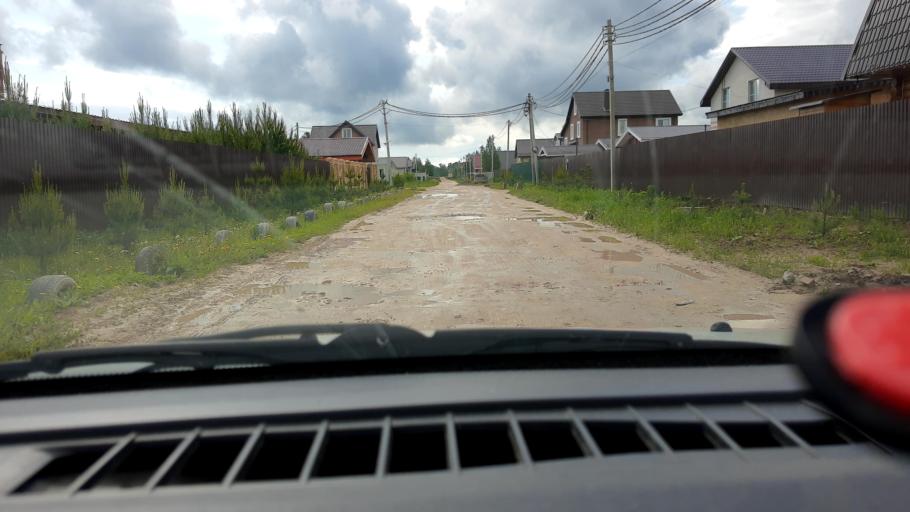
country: RU
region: Nizjnij Novgorod
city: Neklyudovo
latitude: 56.4314
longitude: 43.9641
